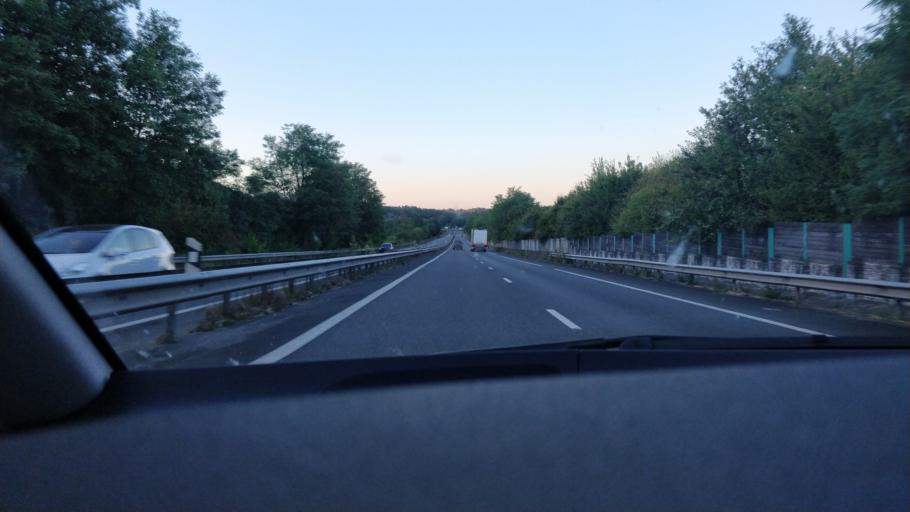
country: FR
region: Poitou-Charentes
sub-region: Departement de la Charente
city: Taponnat-Fleurignac
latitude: 45.7711
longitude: 0.4004
